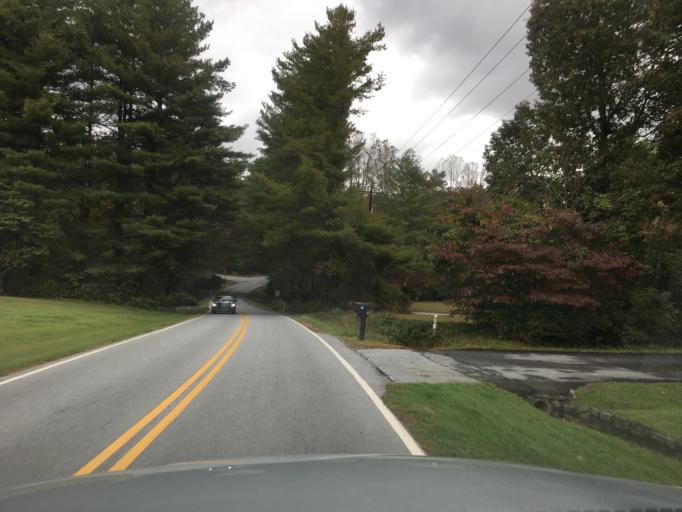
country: US
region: North Carolina
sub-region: Henderson County
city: Valley Hill
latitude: 35.2953
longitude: -82.4963
